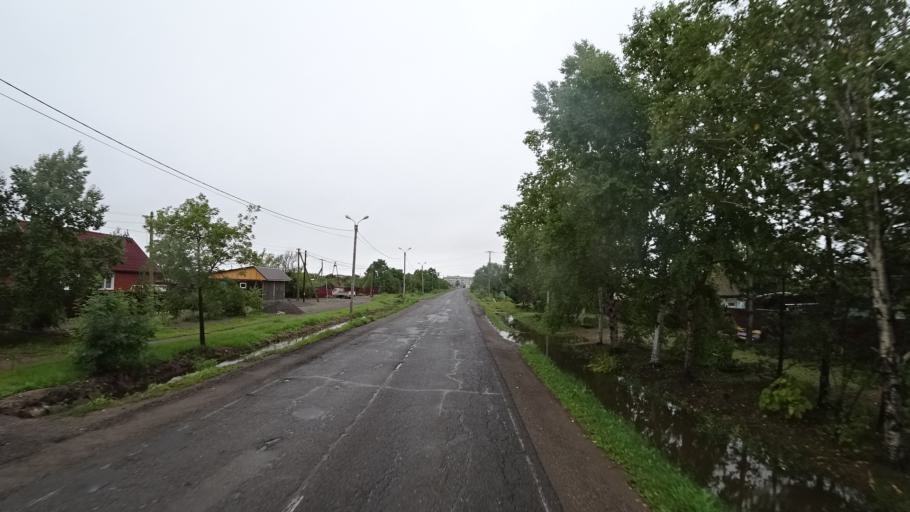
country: RU
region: Primorskiy
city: Monastyrishche
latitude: 44.2017
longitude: 132.4553
